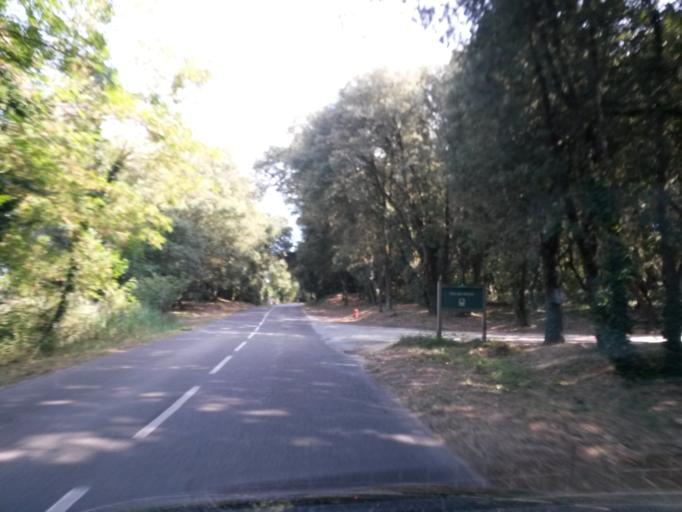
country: FR
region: Pays de la Loire
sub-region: Departement de la Vendee
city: Olonne-sur-Mer
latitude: 46.5294
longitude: -1.8119
